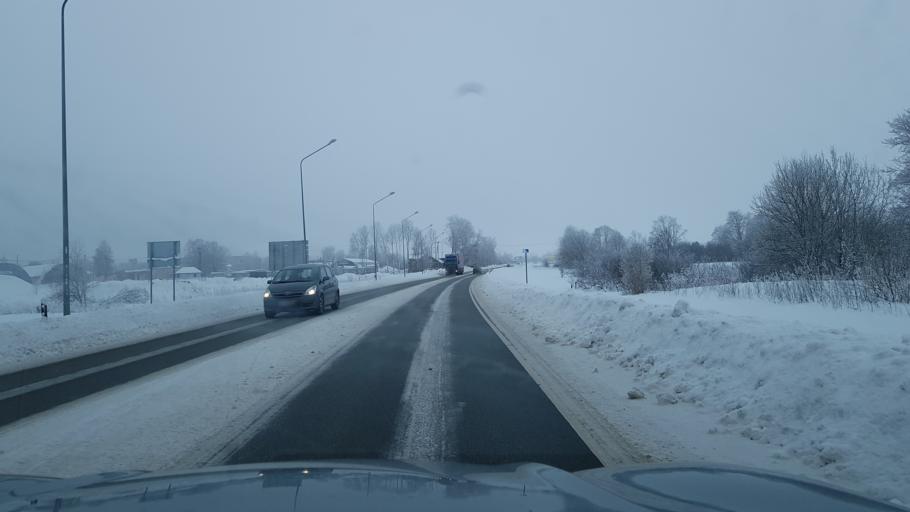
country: EE
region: Ida-Virumaa
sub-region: Johvi vald
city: Johvi
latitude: 59.3354
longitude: 27.4029
